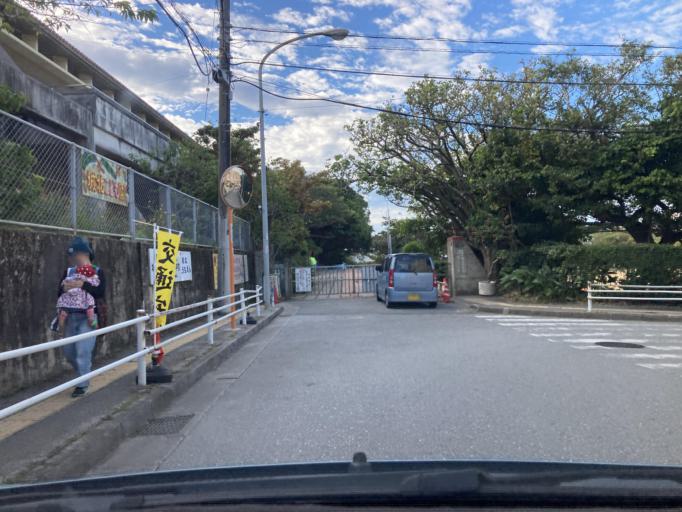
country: JP
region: Okinawa
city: Naha-shi
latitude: 26.2279
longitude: 127.7219
